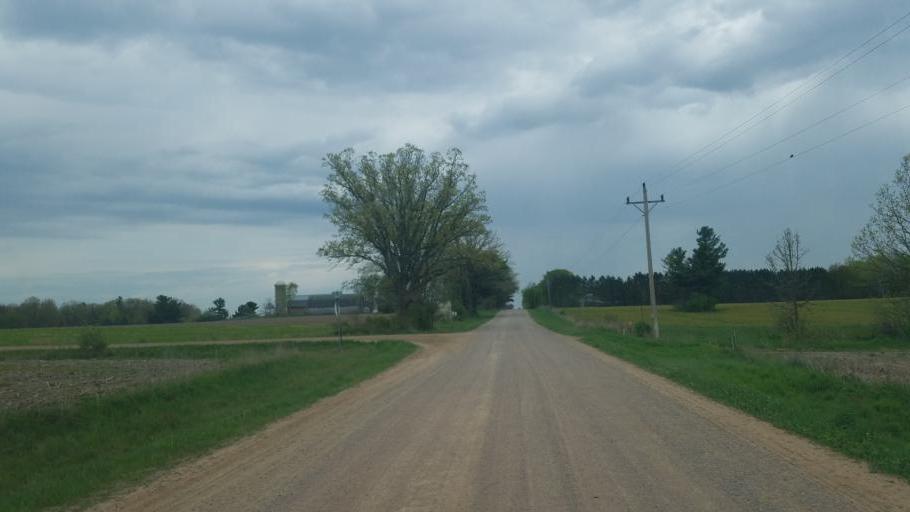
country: US
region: Wisconsin
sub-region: Clark County
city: Loyal
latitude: 44.6259
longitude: -90.4361
